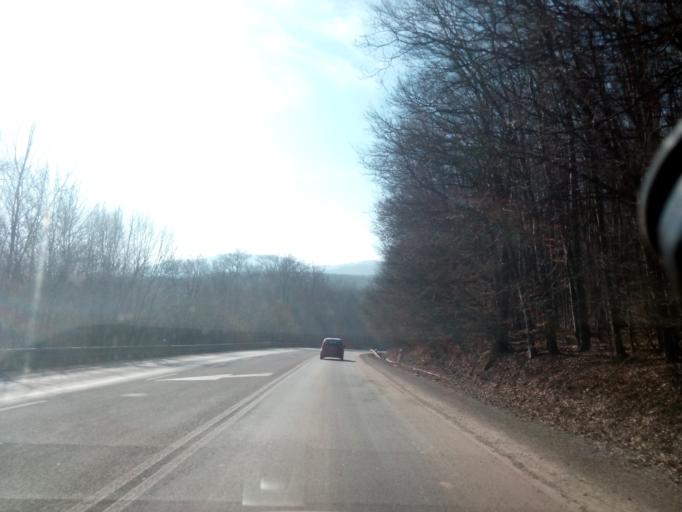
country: SK
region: Kosicky
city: Secovce
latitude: 48.7372
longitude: 21.5368
